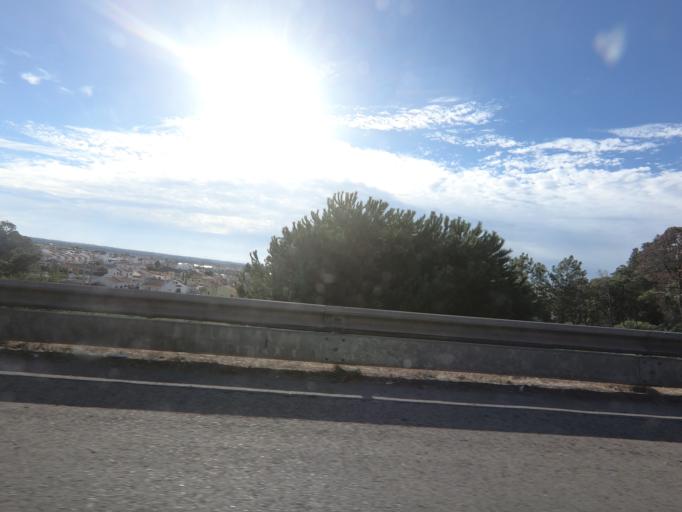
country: PT
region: Setubal
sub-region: Barreiro
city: Santo Antonio da Charneca
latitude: 38.6326
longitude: -9.0438
